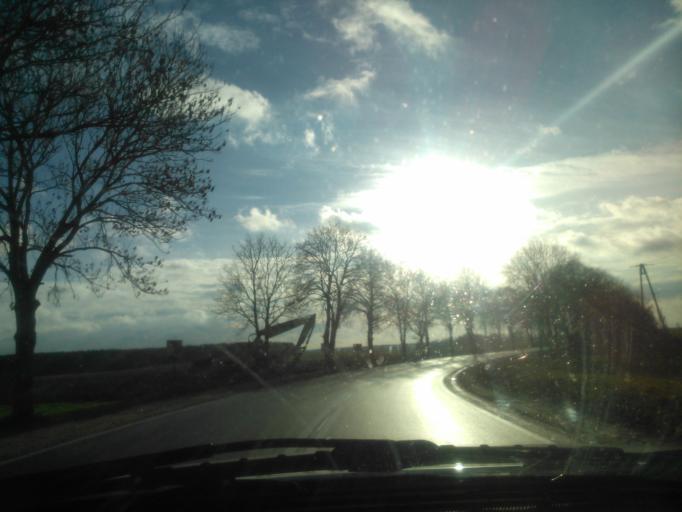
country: PL
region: Podlasie
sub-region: Powiat kolnenski
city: Maly Plock
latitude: 53.3278
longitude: 22.0198
